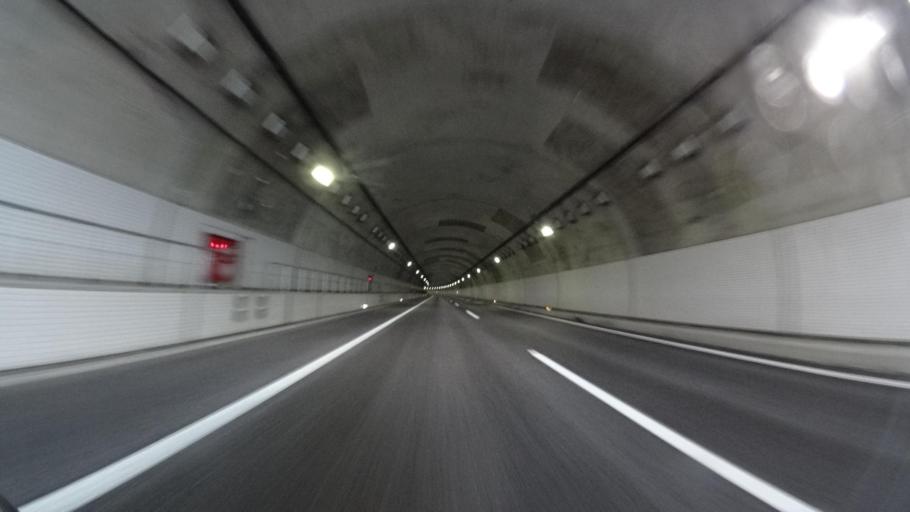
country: JP
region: Mie
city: Kameyama
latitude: 34.9136
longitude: 136.4265
